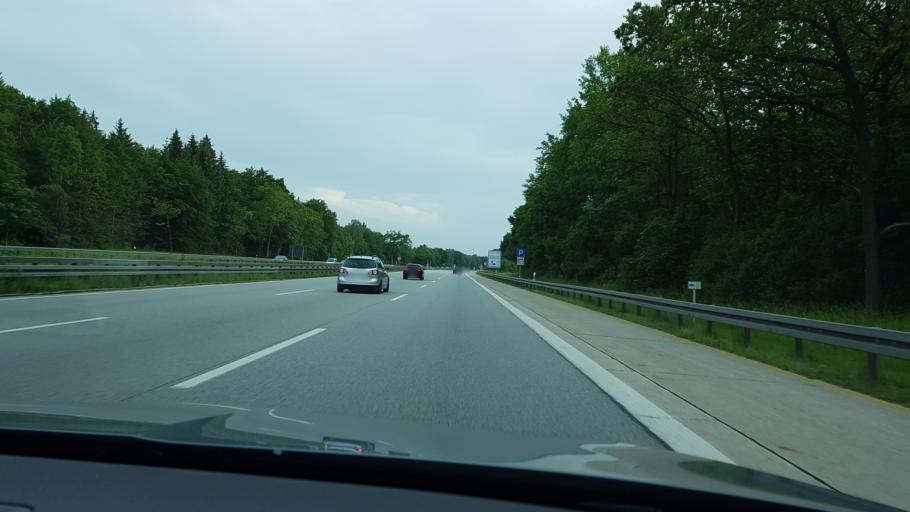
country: DE
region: Bavaria
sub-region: Upper Bavaria
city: Schaftlarn
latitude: 48.0348
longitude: 11.4297
